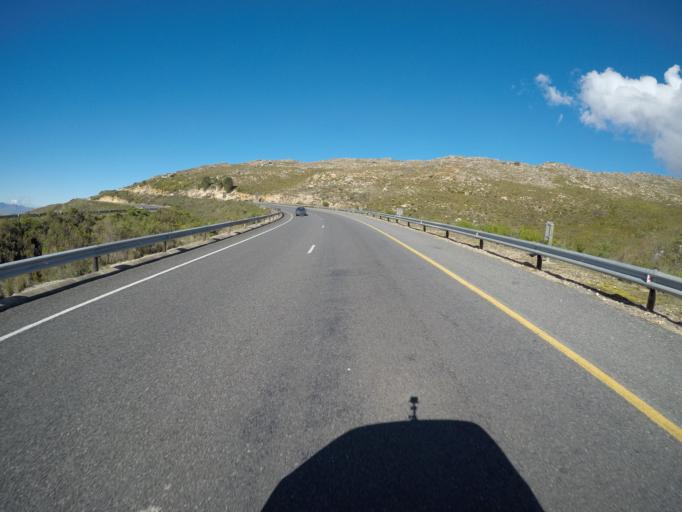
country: ZA
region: Western Cape
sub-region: Overberg District Municipality
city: Grabouw
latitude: -34.2129
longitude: 19.1624
